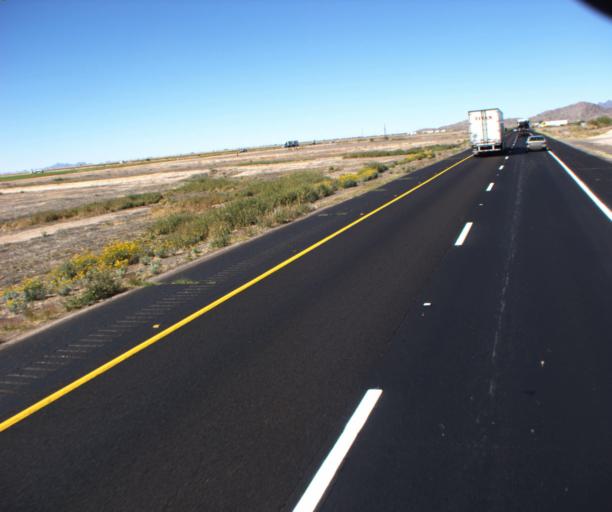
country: US
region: Arizona
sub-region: Maricopa County
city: Buckeye
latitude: 33.3877
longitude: -112.6253
